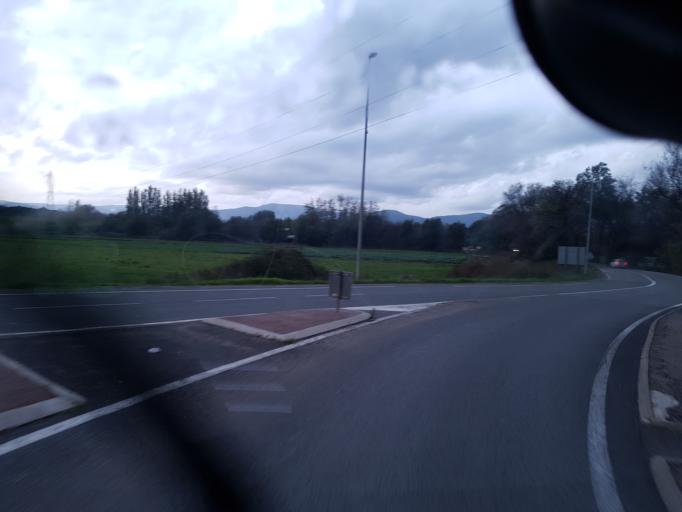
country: FR
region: Provence-Alpes-Cote d'Azur
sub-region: Departement du Var
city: Gassin
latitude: 43.2597
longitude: 6.5688
